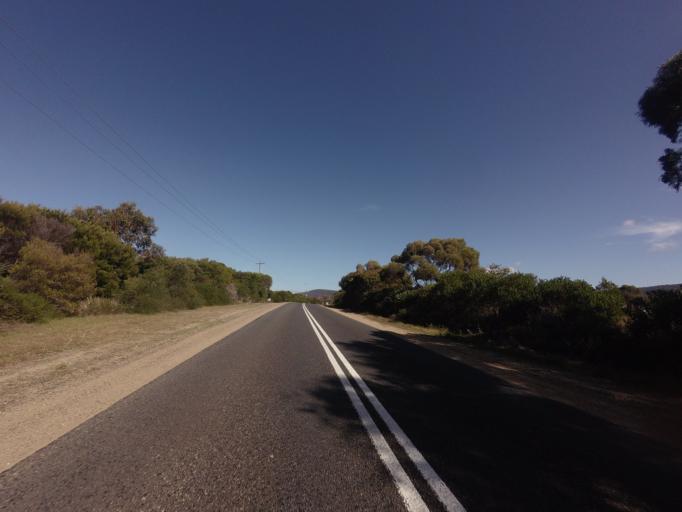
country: AU
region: Tasmania
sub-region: Break O'Day
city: St Helens
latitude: -41.8210
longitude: 148.2630
